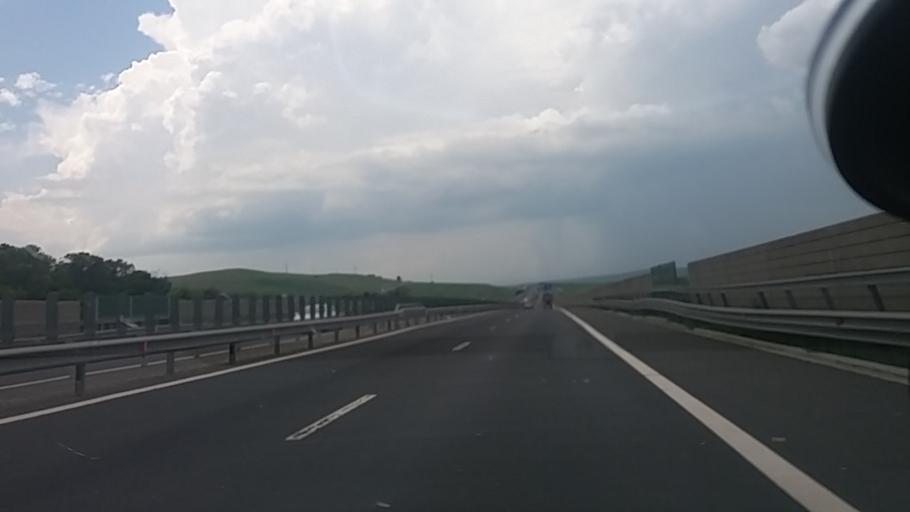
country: RO
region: Alba
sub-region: Comuna Garbova
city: Garbova
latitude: 45.9086
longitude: 23.7431
